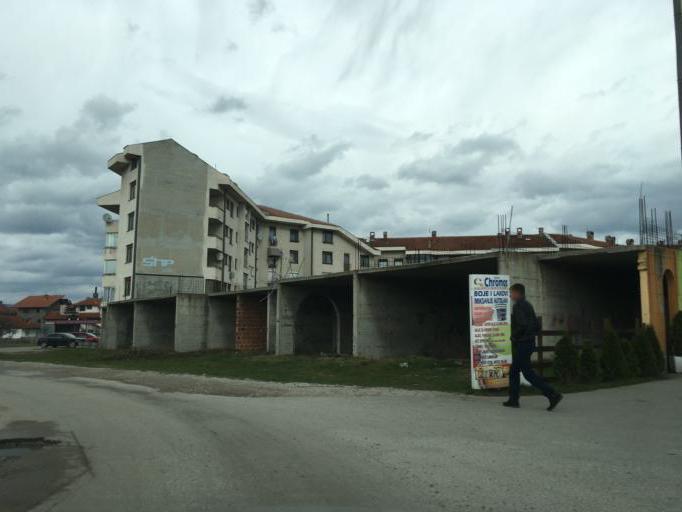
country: BA
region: Federation of Bosnia and Herzegovina
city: Bugojno
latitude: 44.0516
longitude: 17.4515
